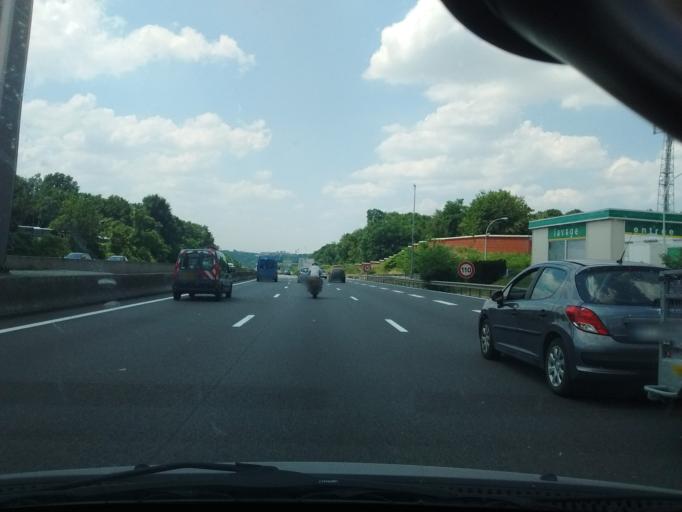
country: FR
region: Ile-de-France
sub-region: Departement de l'Essonne
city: Etiolles
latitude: 48.6306
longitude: 2.4861
